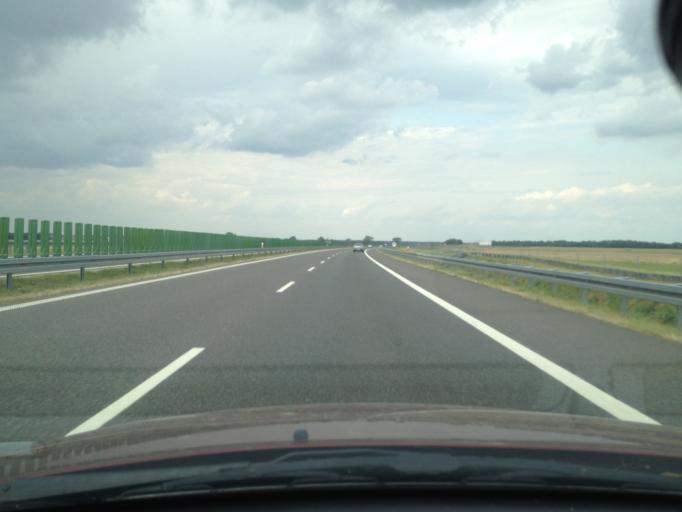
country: PL
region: West Pomeranian Voivodeship
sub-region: Powiat pyrzycki
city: Kozielice
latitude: 53.1065
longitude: 14.7632
